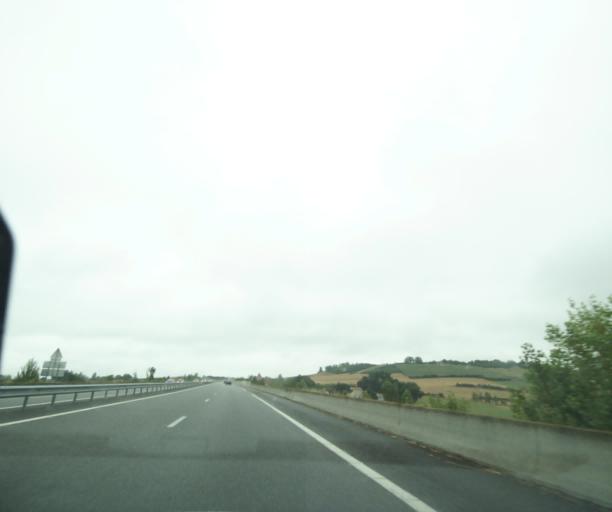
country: FR
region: Midi-Pyrenees
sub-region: Departement du Tarn
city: Le Garric
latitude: 44.0145
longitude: 2.1806
